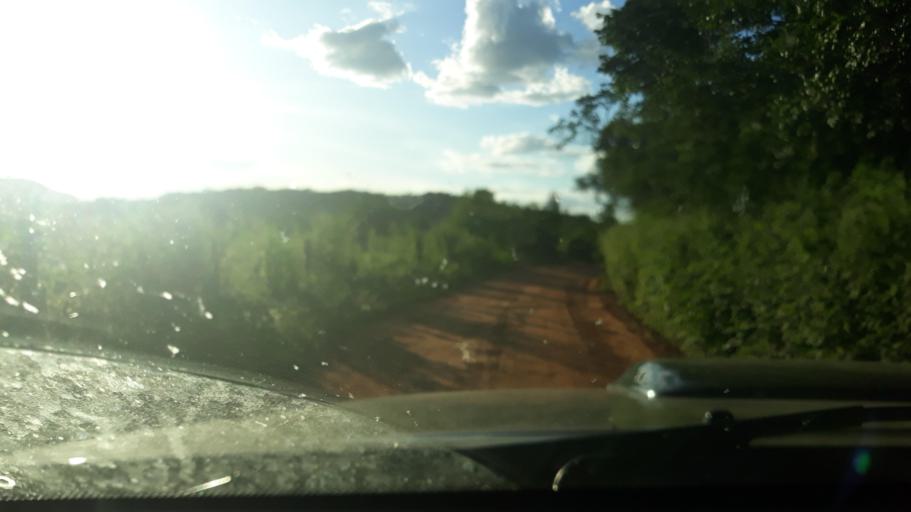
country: BR
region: Bahia
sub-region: Riacho De Santana
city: Riacho de Santana
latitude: -13.8458
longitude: -42.7640
